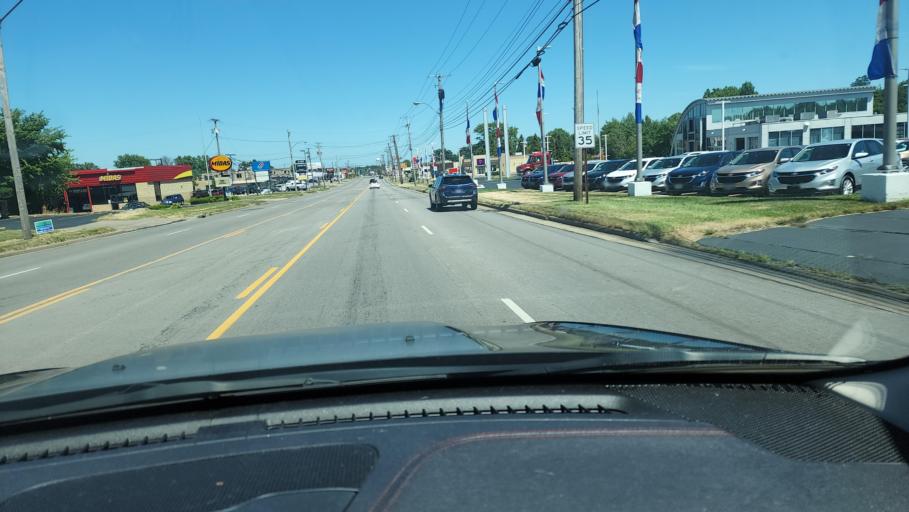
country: US
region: Ohio
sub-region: Mahoning County
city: Austintown
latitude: 41.1011
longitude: -80.7397
